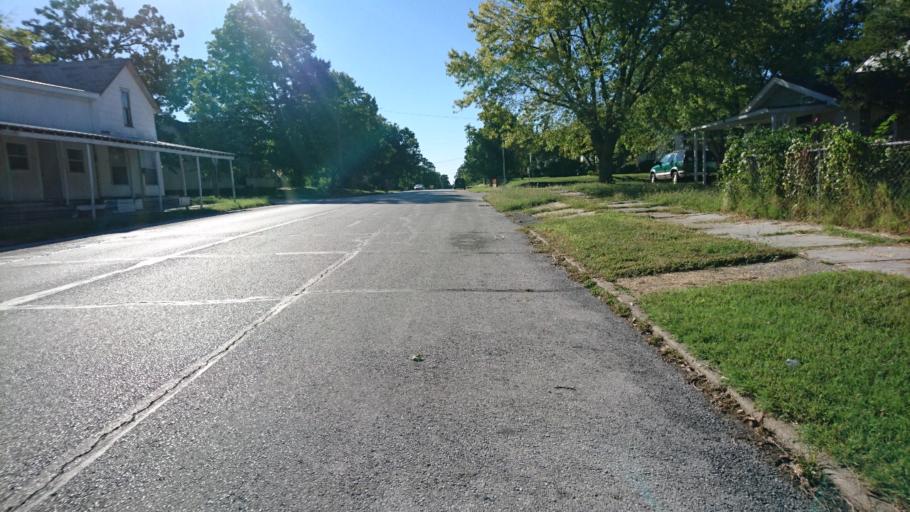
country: US
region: Missouri
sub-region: Jasper County
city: Carthage
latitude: 37.1765
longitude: -94.3196
